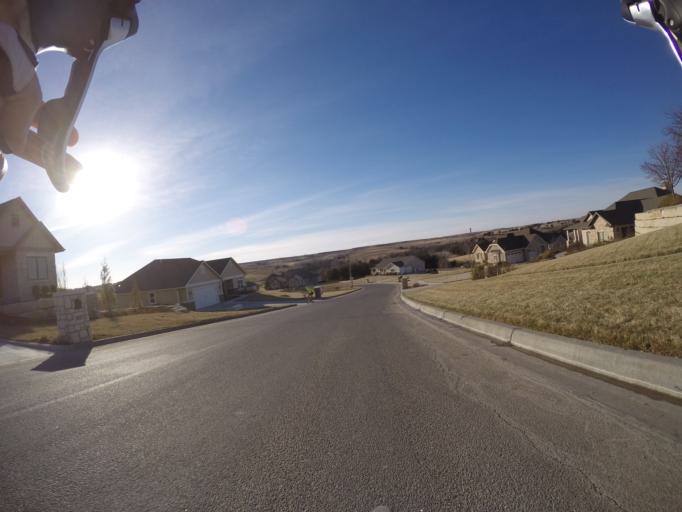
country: US
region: Kansas
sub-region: Riley County
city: Manhattan
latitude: 39.2129
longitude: -96.6296
